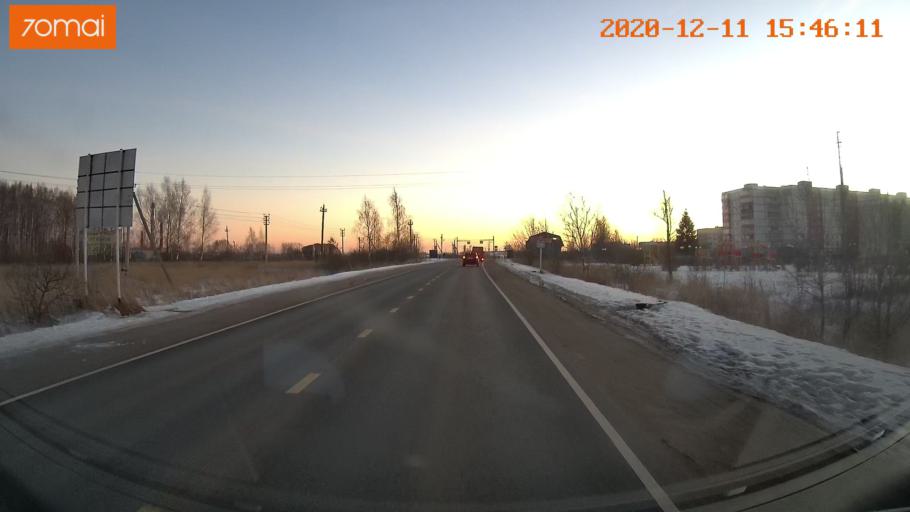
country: RU
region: Ivanovo
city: Novo-Talitsy
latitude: 57.0069
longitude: 40.8543
